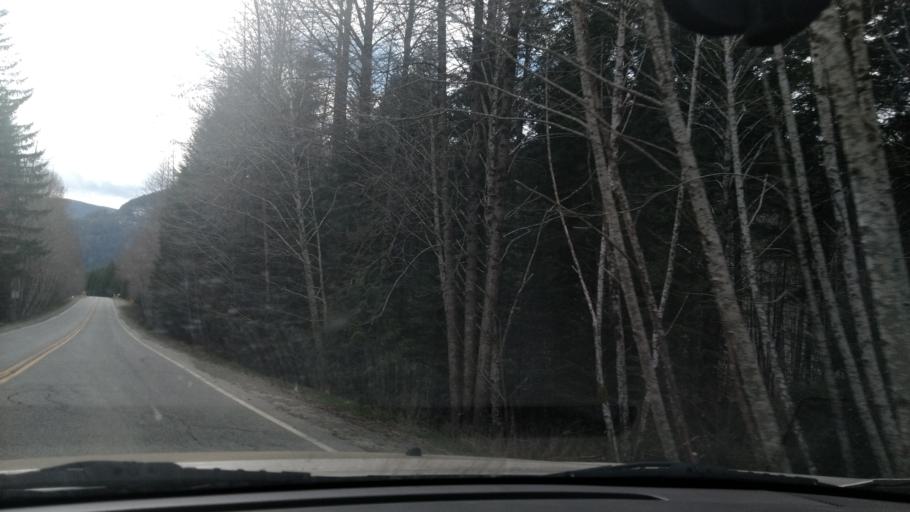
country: CA
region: British Columbia
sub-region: Regional District of Alberni-Clayoquot
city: Tofino
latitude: 49.8364
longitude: -125.9452
